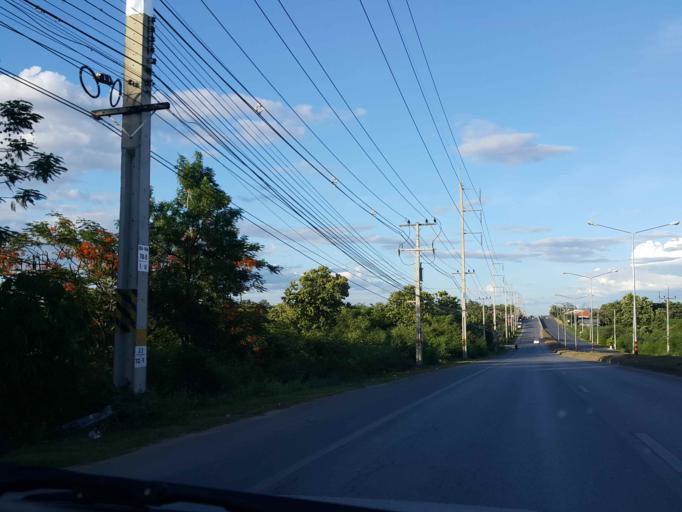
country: TH
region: Chiang Mai
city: Chom Thong
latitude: 18.4450
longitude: 98.6965
